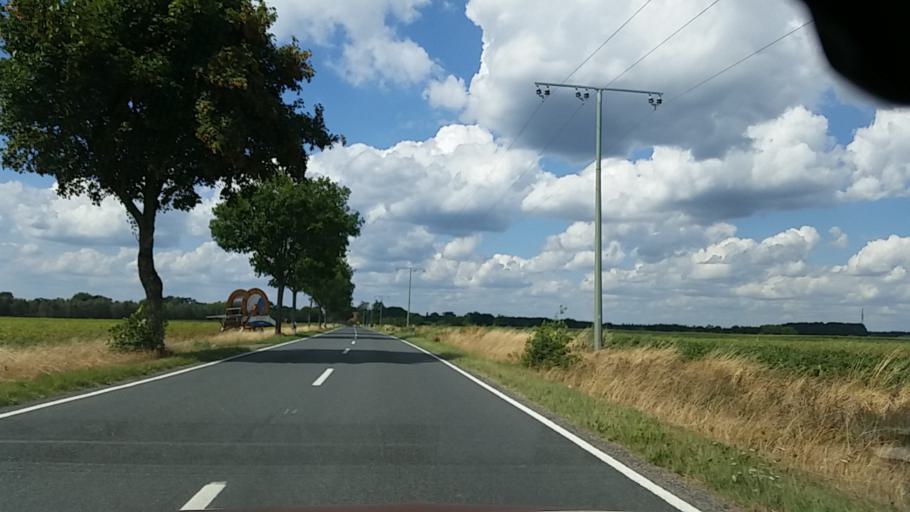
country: DE
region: Lower Saxony
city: Sprakensehl
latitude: 52.7612
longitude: 10.5024
